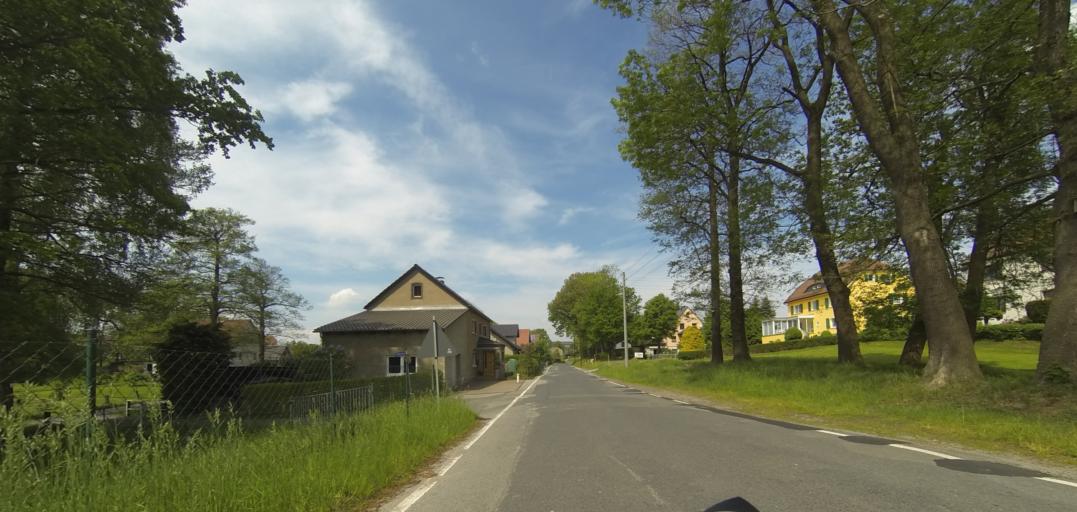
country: DE
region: Saxony
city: Grossrohrsdorf
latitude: 51.0985
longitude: 14.0467
